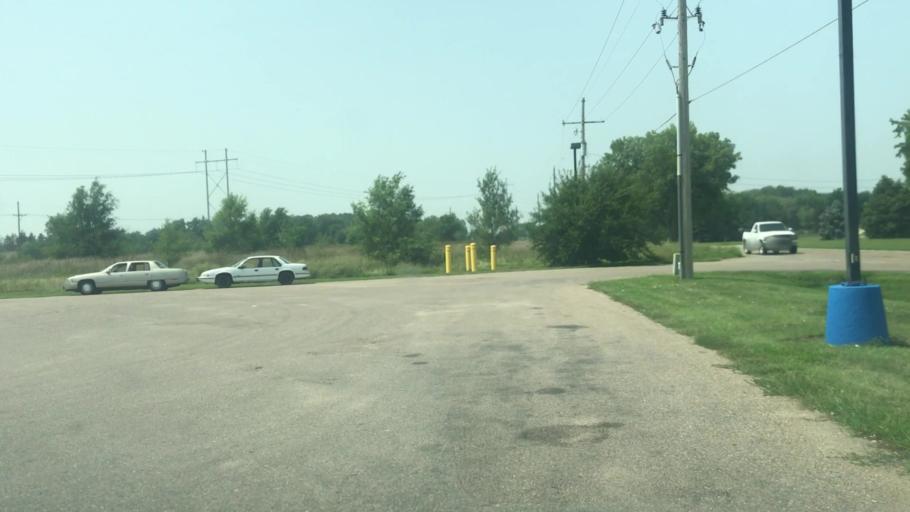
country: US
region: Nebraska
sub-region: Hall County
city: Grand Island
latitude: 40.9157
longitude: -98.3024
